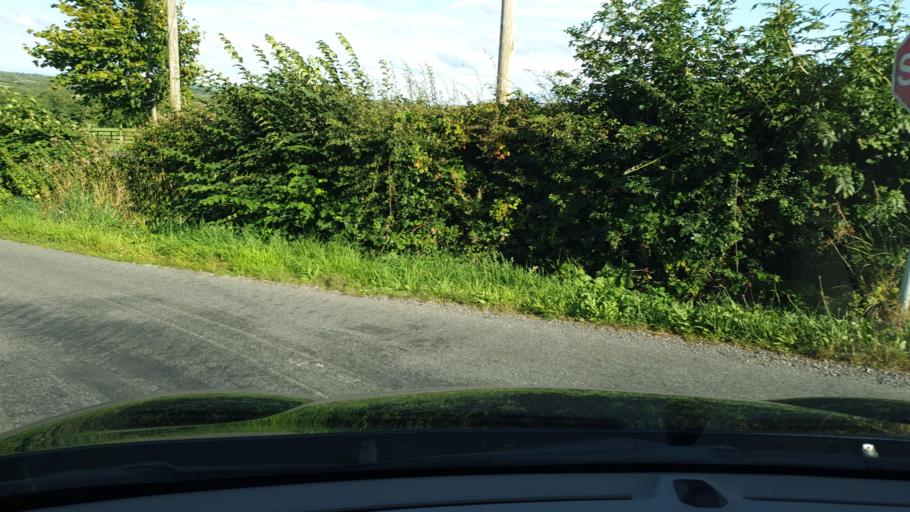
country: IE
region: Leinster
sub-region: An Mhi
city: Stamullin
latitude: 53.6066
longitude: -6.2890
